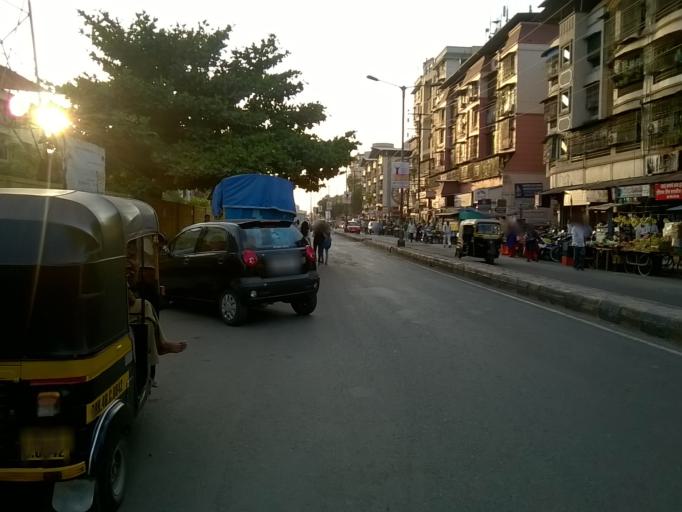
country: IN
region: Maharashtra
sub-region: Raigarh
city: Kalundri
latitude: 18.9902
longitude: 73.1251
